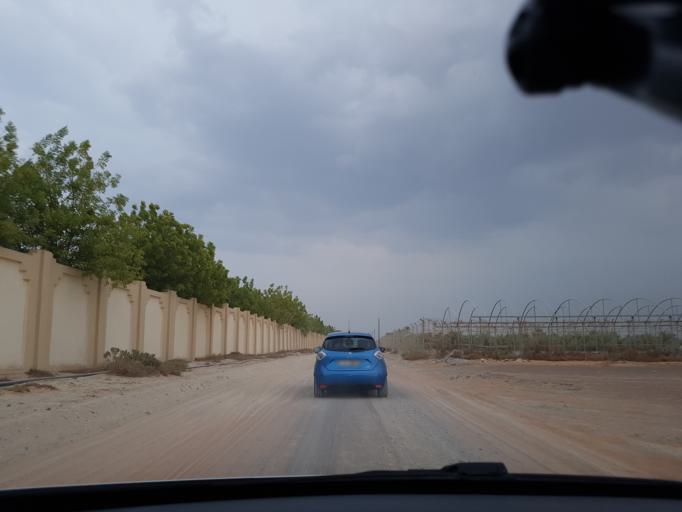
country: AE
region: Ash Shariqah
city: Adh Dhayd
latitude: 25.2759
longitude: 55.9145
